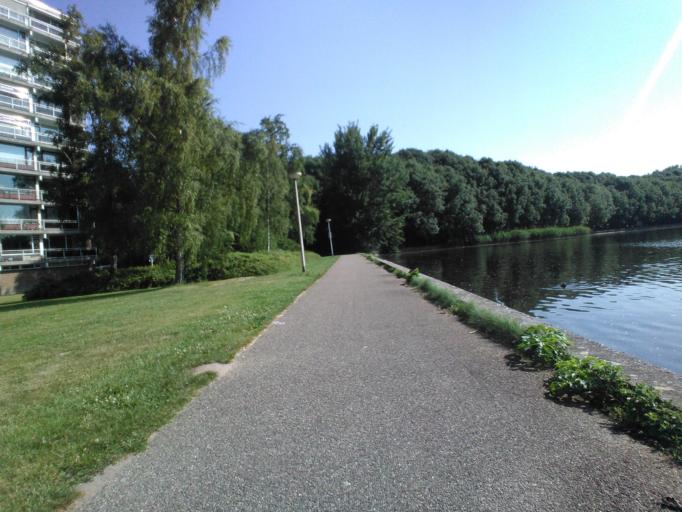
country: NL
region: South Holland
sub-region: Gemeente Alphen aan den Rijn
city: Alphen aan den Rijn
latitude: 52.1413
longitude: 4.6825
